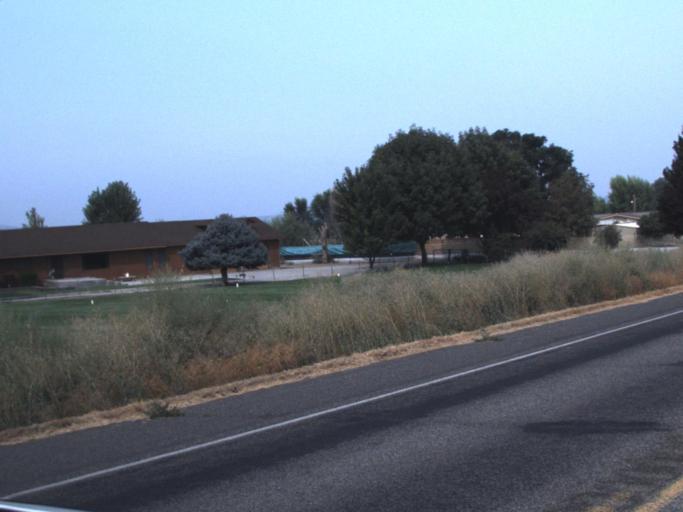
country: US
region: Washington
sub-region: Yakima County
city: Sunnyside
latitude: 46.2794
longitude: -119.9993
